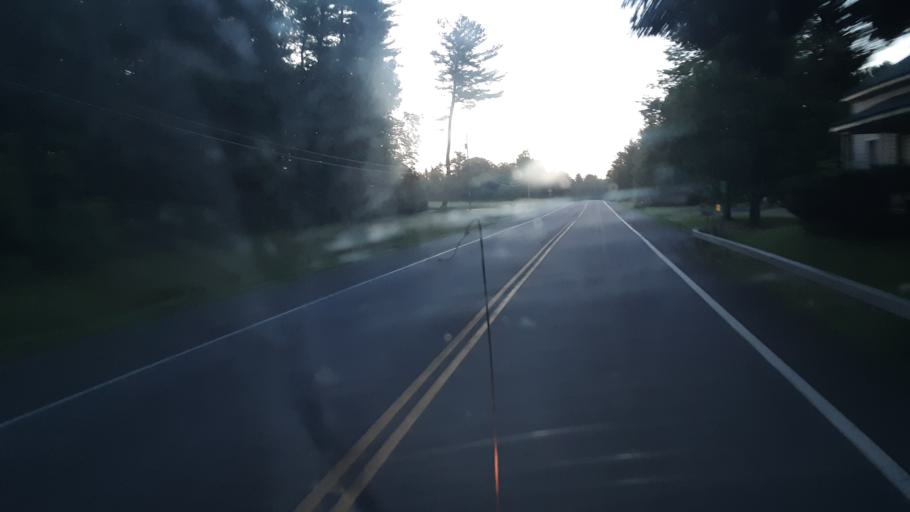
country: US
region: New York
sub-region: Montgomery County
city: Hagaman
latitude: 42.9678
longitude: -74.1123
